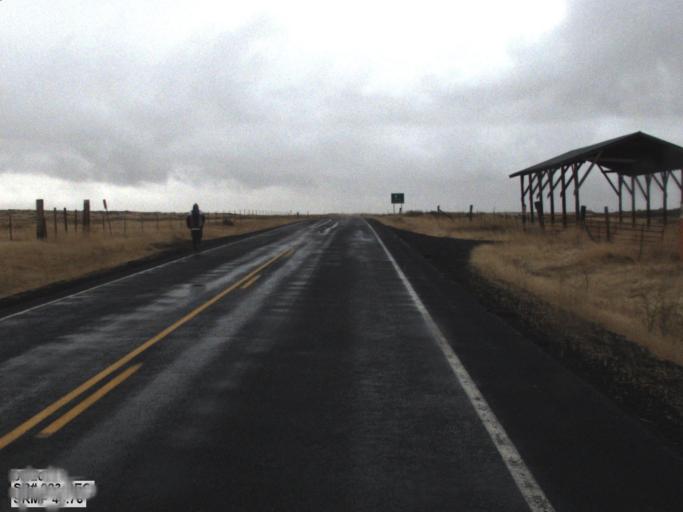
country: US
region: Washington
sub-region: Lincoln County
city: Davenport
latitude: 47.3218
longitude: -117.9798
